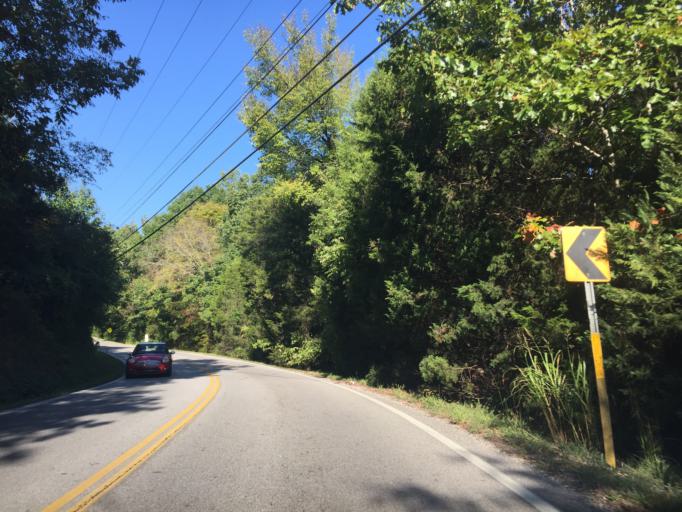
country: US
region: Tennessee
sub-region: Hamilton County
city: Harrison
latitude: 35.1217
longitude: -85.0863
